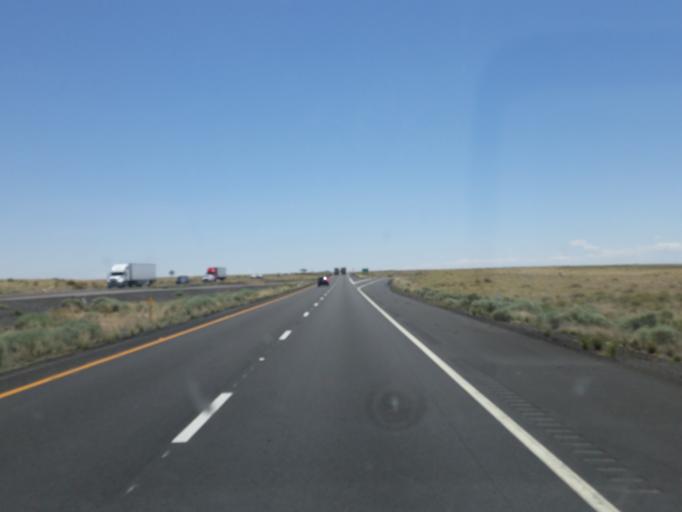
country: US
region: Arizona
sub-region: Coconino County
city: LeChee
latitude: 35.1307
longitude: -111.1887
